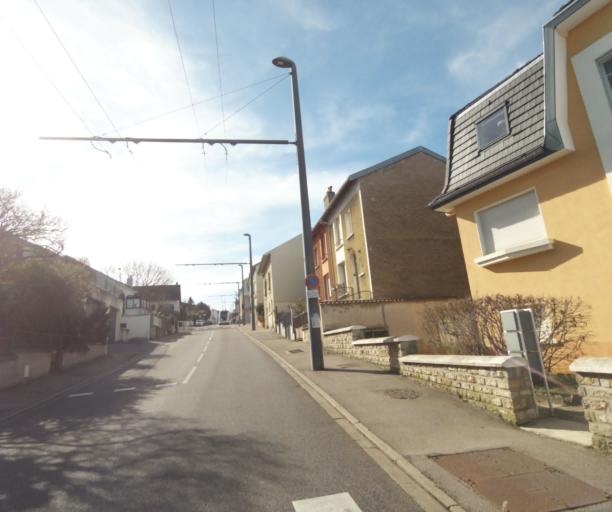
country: FR
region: Lorraine
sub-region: Departement de Meurthe-et-Moselle
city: Villers-les-Nancy
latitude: 48.6634
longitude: 6.1629
